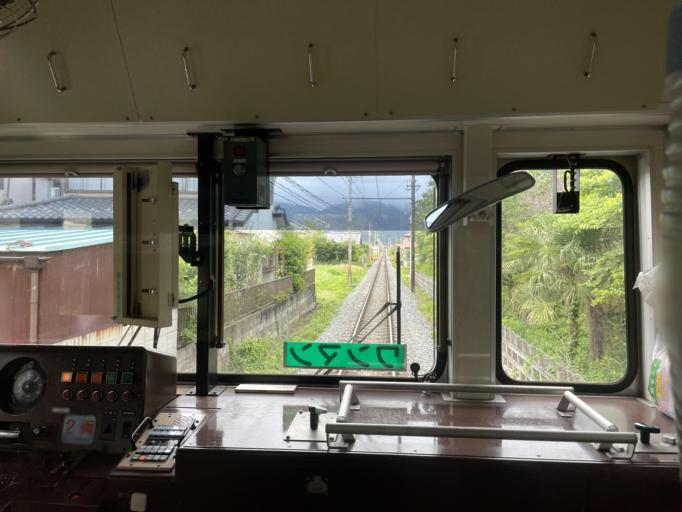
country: JP
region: Saitama
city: Kodamacho-kodamaminami
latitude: 36.1049
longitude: 139.1105
